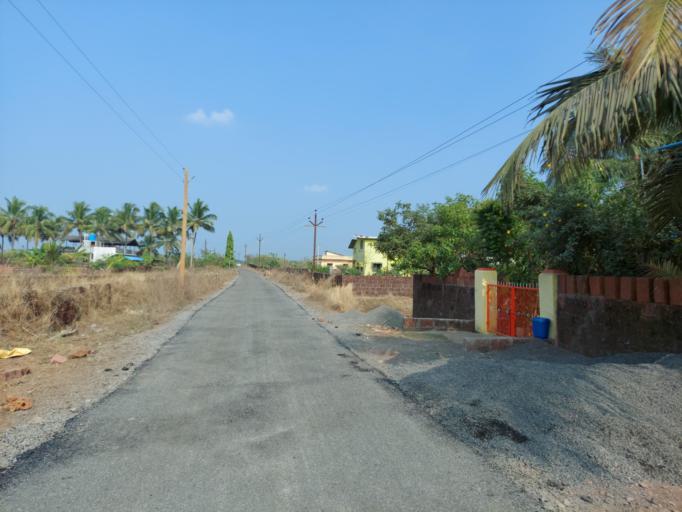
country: IN
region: Maharashtra
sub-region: Ratnagiri
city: Ratnagiri
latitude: 16.9268
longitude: 73.3197
